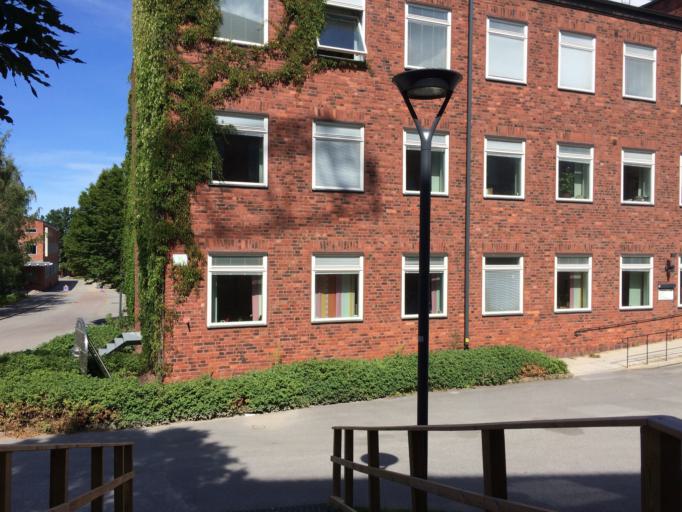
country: SE
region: Stockholm
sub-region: Stockholms Kommun
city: OEstermalm
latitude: 59.3493
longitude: 18.0737
